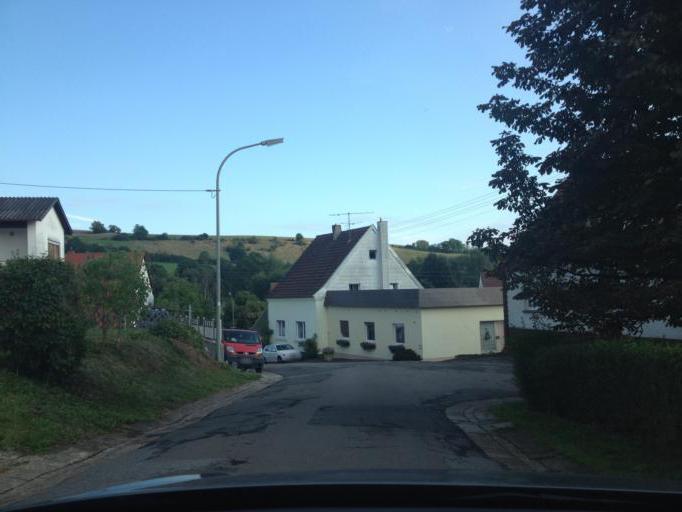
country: DE
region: Rheinland-Pfalz
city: Breitenbach
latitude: 49.4523
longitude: 7.2322
